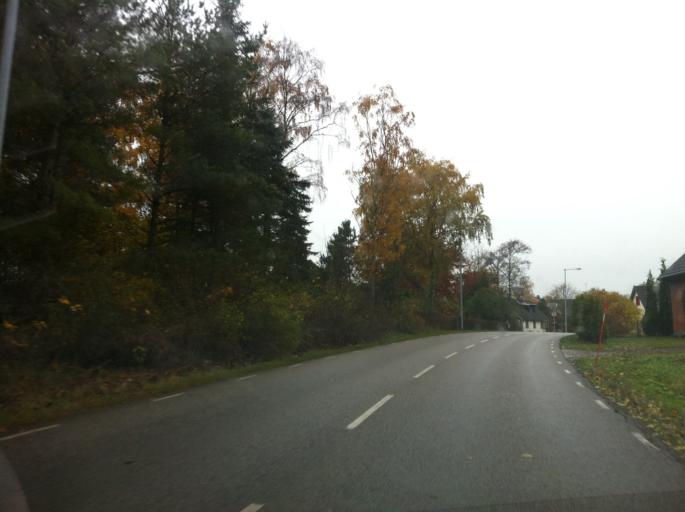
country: SE
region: Skane
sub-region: Kavlinge Kommun
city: Kaevlinge
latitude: 55.8119
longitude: 13.0549
